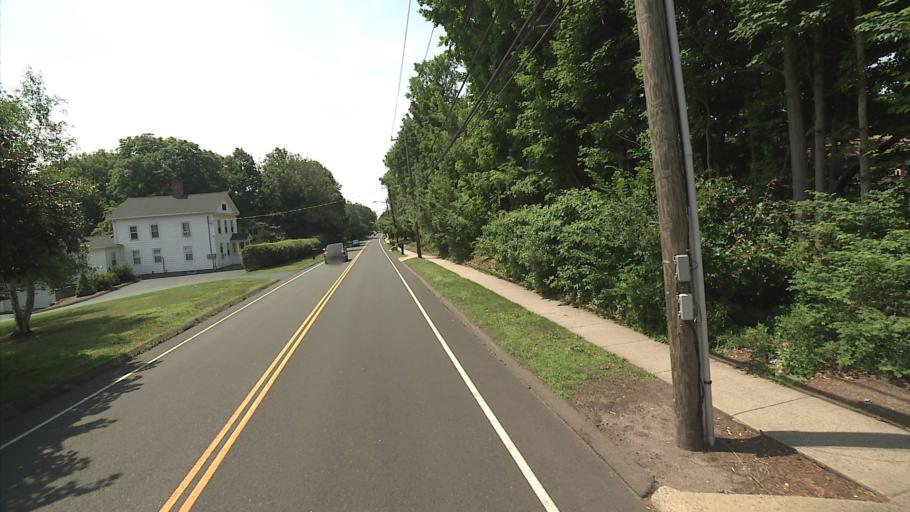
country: US
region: Connecticut
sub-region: New Haven County
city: Branford
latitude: 41.3010
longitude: -72.8192
